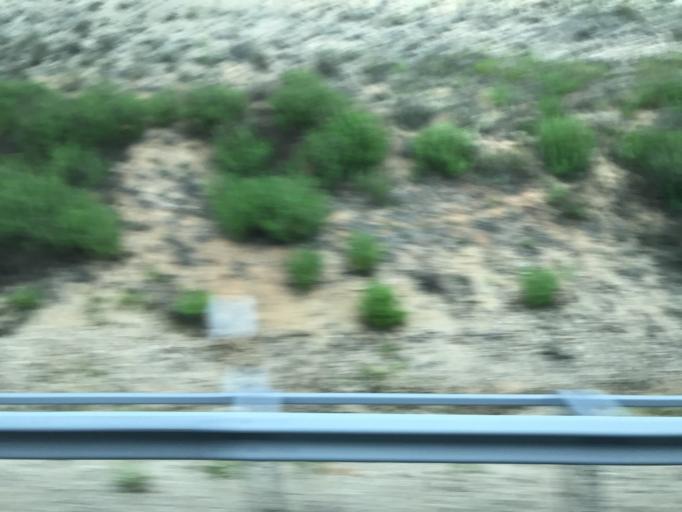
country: ES
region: Castille and Leon
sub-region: Provincia de Burgos
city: Oquillas
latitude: 41.8115
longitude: -3.7009
